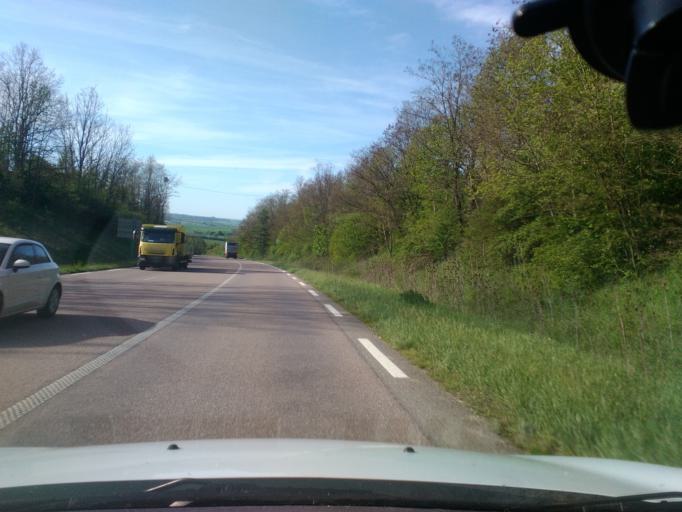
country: FR
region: Lorraine
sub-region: Departement des Vosges
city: Mirecourt
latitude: 48.2815
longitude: 6.1496
